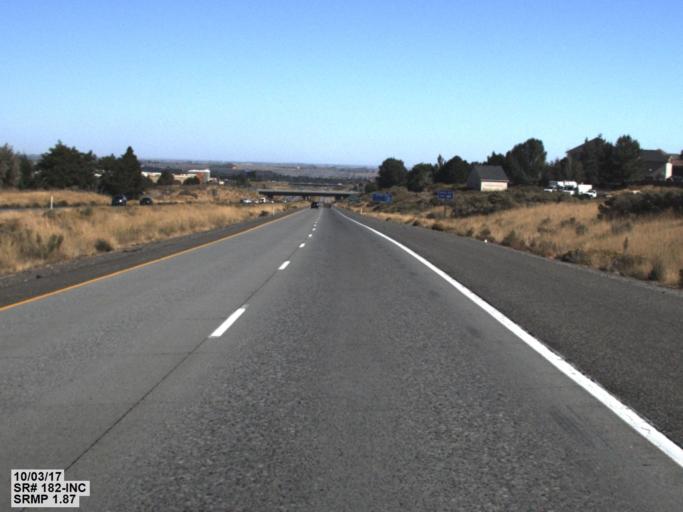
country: US
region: Washington
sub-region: Benton County
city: Richland
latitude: 46.2479
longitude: -119.3242
